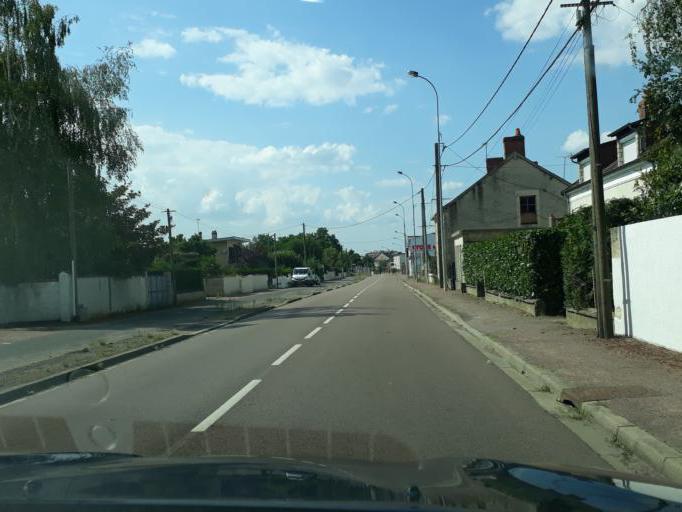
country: FR
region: Bourgogne
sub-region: Departement de la Nievre
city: Fourchambault
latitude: 47.0109
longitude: 3.0902
